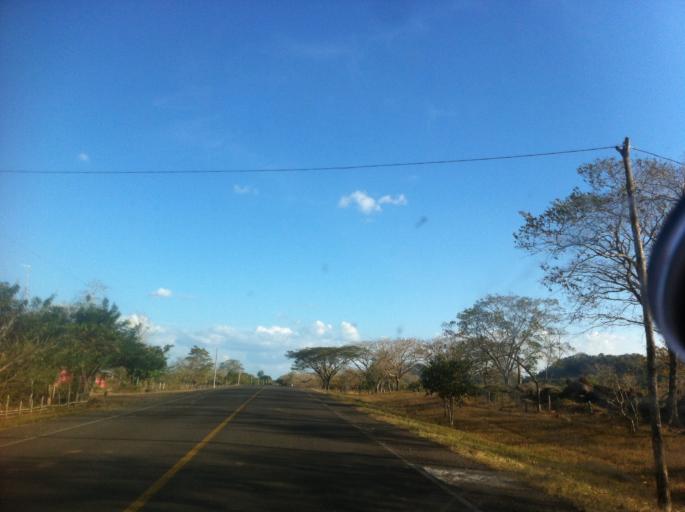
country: NI
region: Rio San Juan
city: Morrito
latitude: 11.7814
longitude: -85.0201
